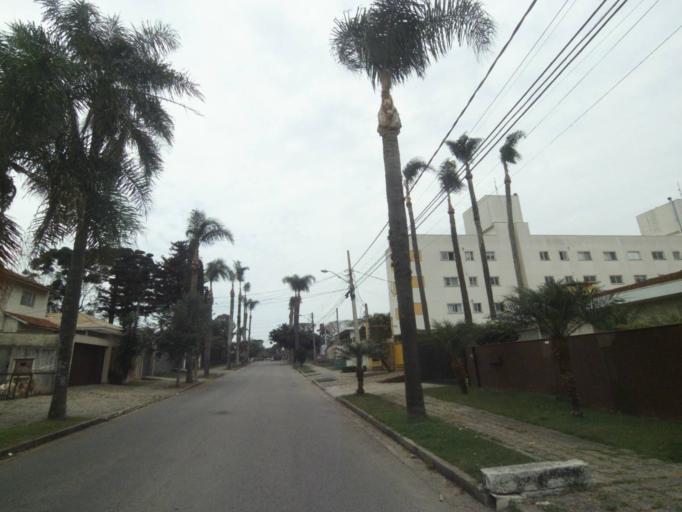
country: BR
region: Parana
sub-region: Curitiba
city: Curitiba
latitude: -25.4567
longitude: -49.3087
